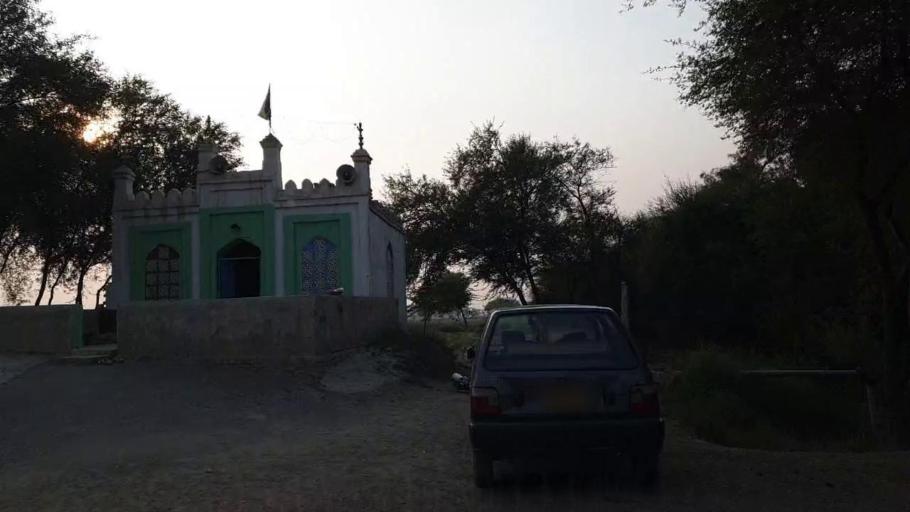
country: PK
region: Sindh
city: Bhan
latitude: 26.4966
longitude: 67.7275
